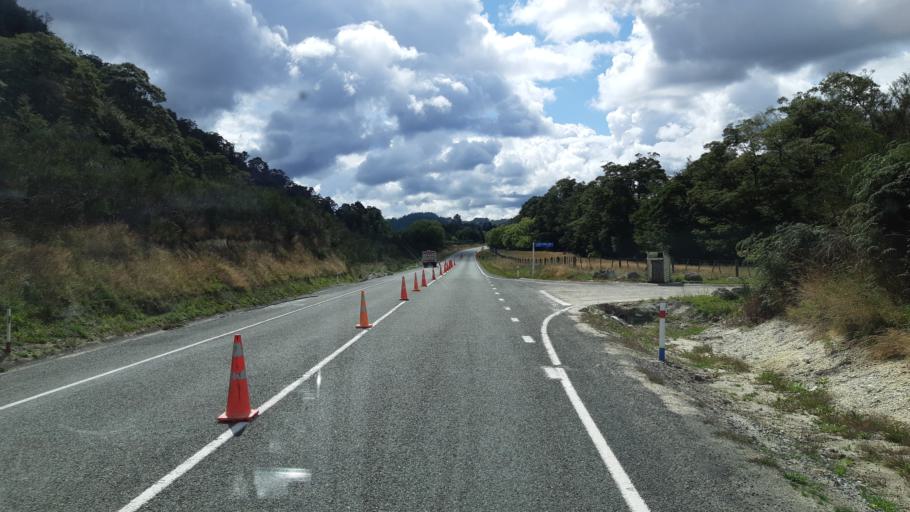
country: NZ
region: Tasman
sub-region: Tasman District
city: Wakefield
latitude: -41.6531
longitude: 172.6456
